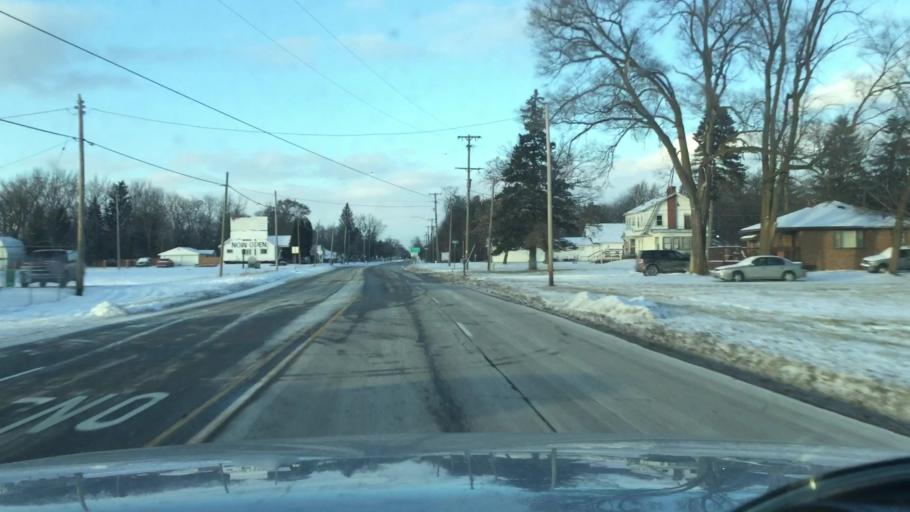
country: US
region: Michigan
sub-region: Saginaw County
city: Saginaw
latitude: 43.3917
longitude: -83.9358
